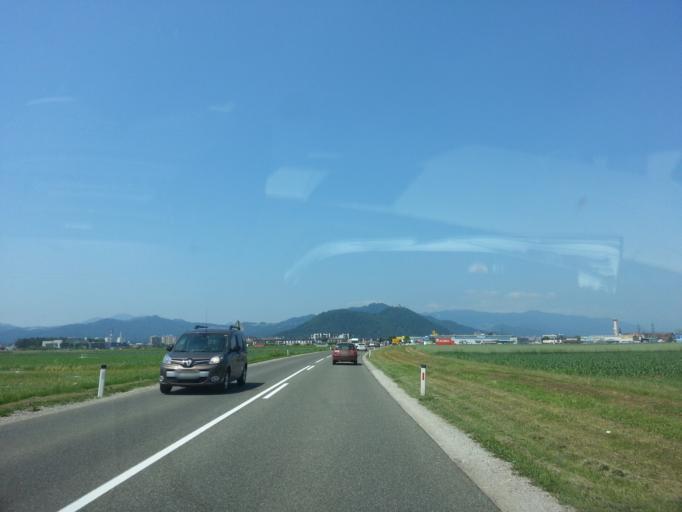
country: SI
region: Kranj
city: Britof
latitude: 46.2417
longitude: 14.3880
